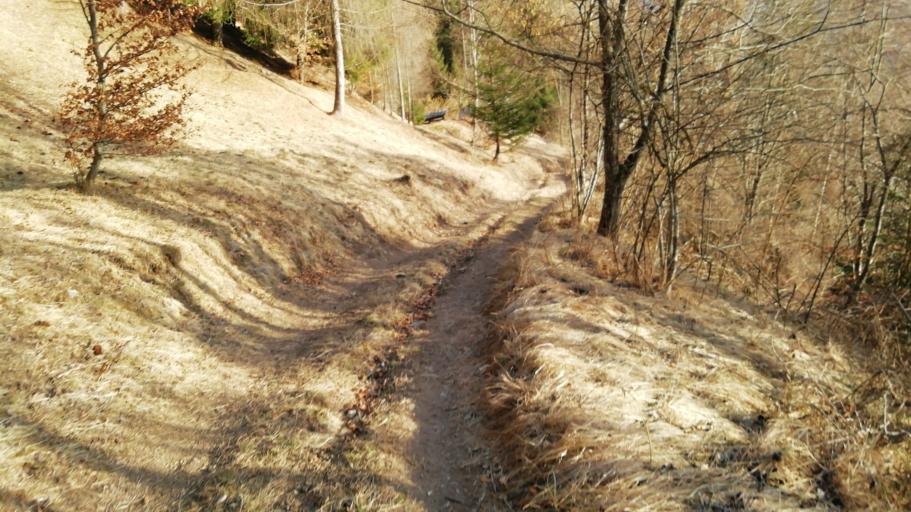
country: IT
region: Veneto
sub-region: Provincia di Belluno
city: Valle di Cadore
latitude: 46.4212
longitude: 12.3165
